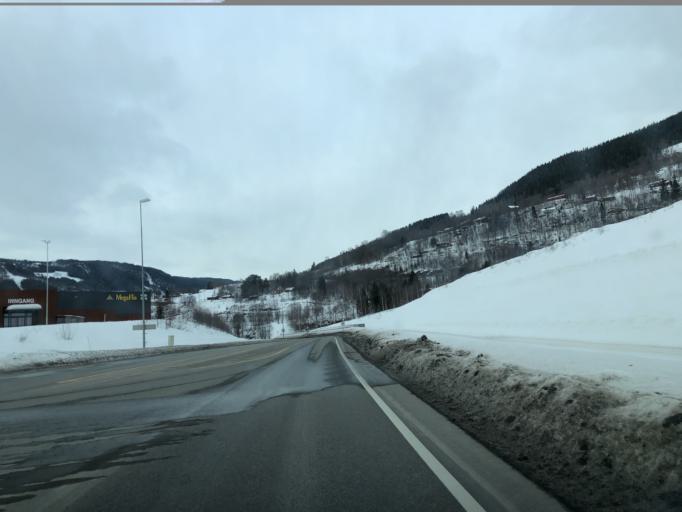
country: NO
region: Oppland
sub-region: Lillehammer
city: Lillehammer
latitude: 61.1496
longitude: 10.4128
